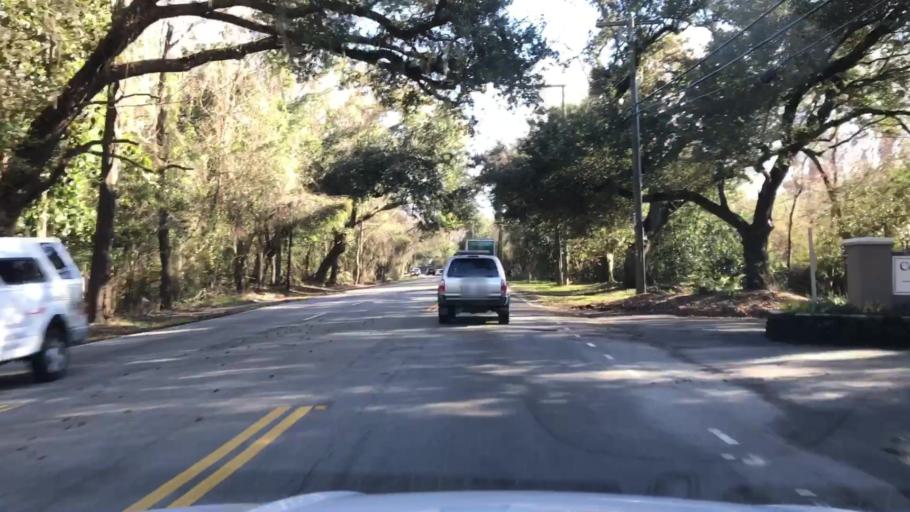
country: US
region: South Carolina
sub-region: Charleston County
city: North Charleston
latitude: 32.8150
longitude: -80.0316
